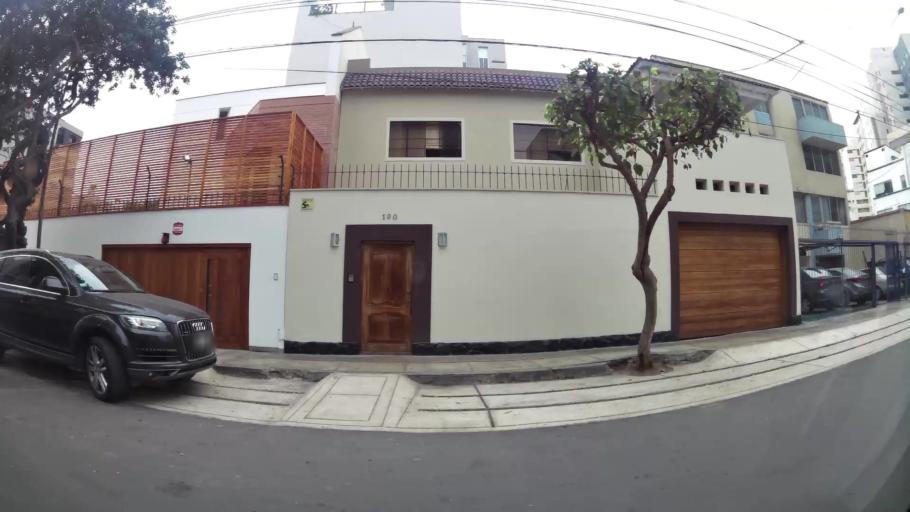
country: PE
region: Lima
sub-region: Lima
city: San Isidro
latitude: -12.1250
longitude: -77.0345
